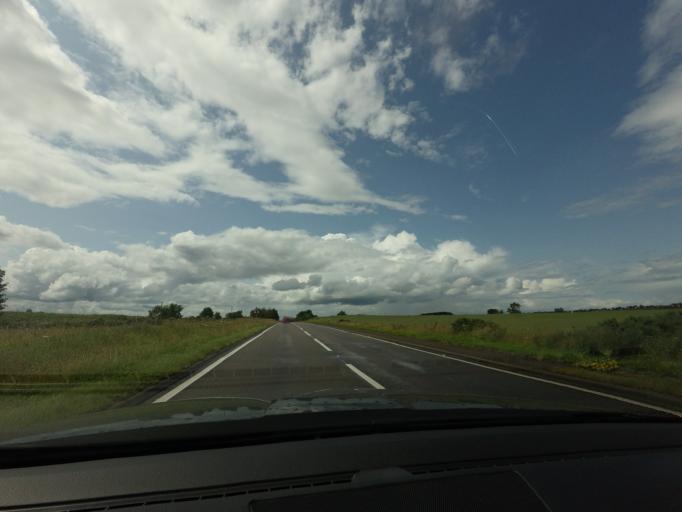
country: GB
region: Scotland
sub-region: Moray
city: Lhanbryd
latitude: 57.6326
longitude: -3.2083
